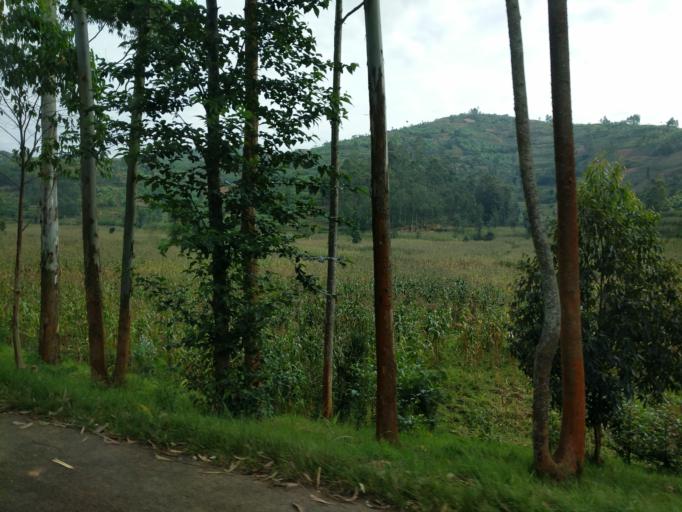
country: RW
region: Northern Province
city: Musanze
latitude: -1.5752
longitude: 29.7199
